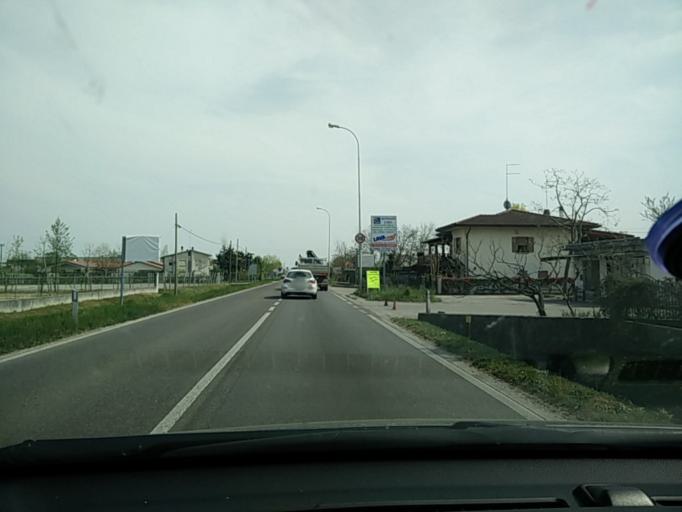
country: IT
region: Veneto
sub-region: Provincia di Treviso
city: Codogne
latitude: 45.8587
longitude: 12.4143
